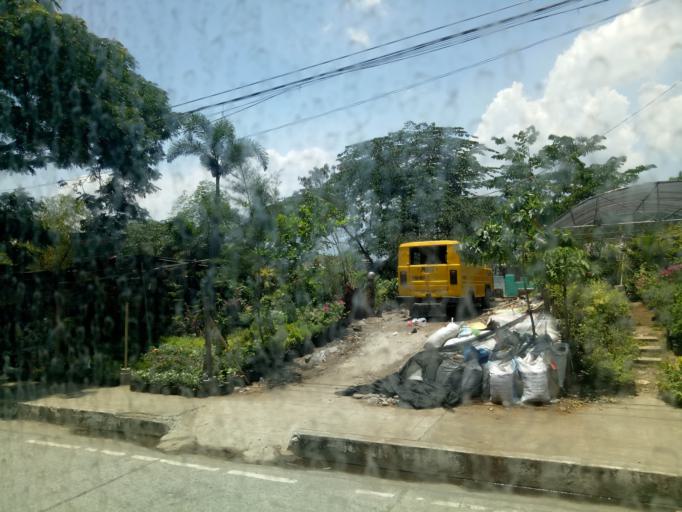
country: PH
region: Calabarzon
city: Bagong Pagasa
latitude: 14.7223
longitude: 121.0512
